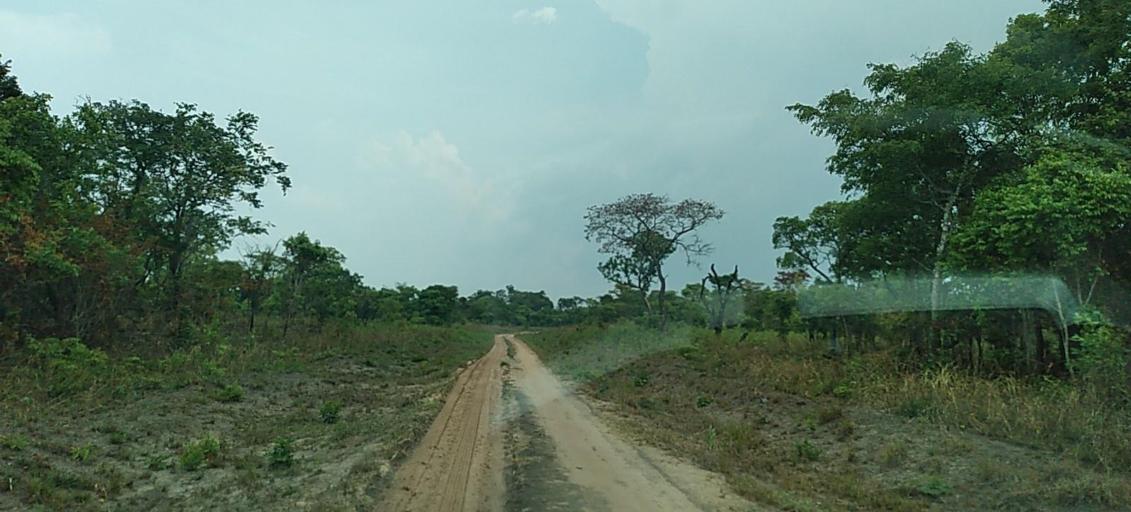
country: ZM
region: North-Western
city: Mwinilunga
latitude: -11.4321
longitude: 24.5934
